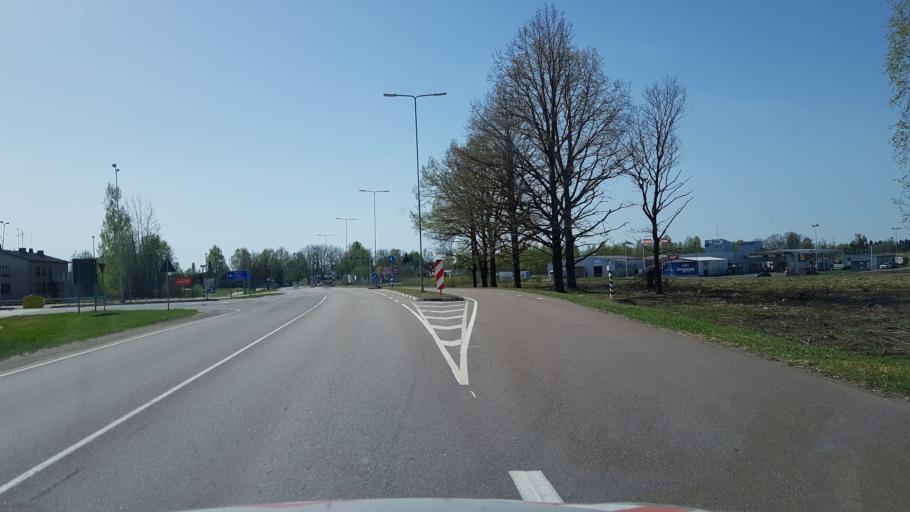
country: EE
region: Valgamaa
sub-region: Valga linn
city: Valga
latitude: 57.7929
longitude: 26.0335
